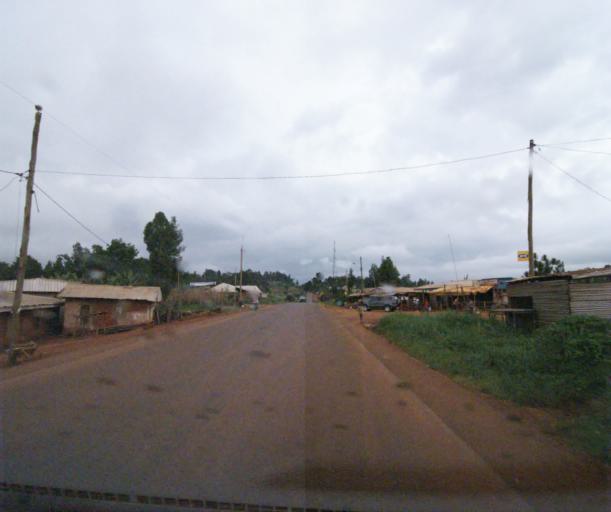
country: CM
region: West
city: Dschang
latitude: 5.4894
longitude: 10.1768
